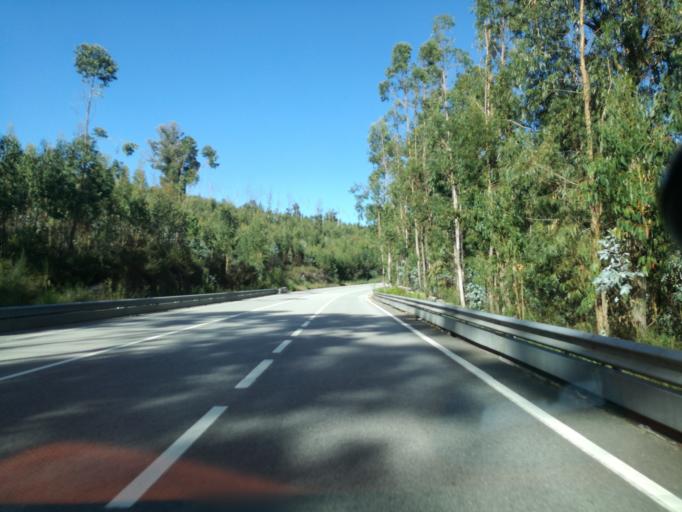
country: PT
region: Porto
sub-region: Pacos de Ferreira
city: Seroa
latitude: 41.2732
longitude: -8.4328
